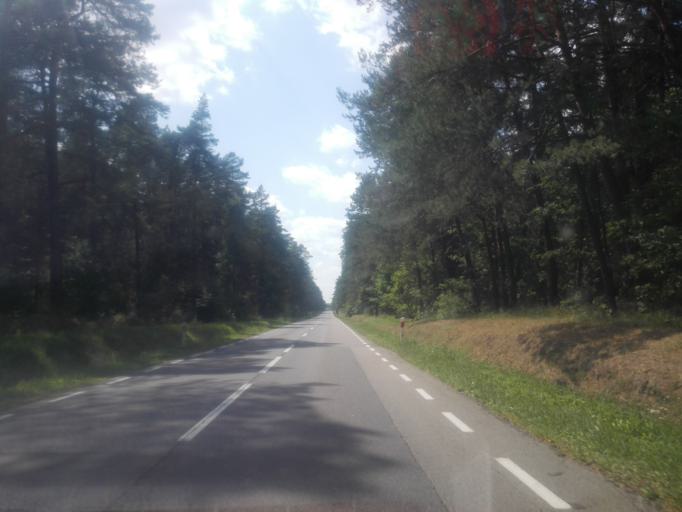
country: PL
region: Podlasie
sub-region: Powiat augustowski
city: Augustow
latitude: 53.8471
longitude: 23.0198
